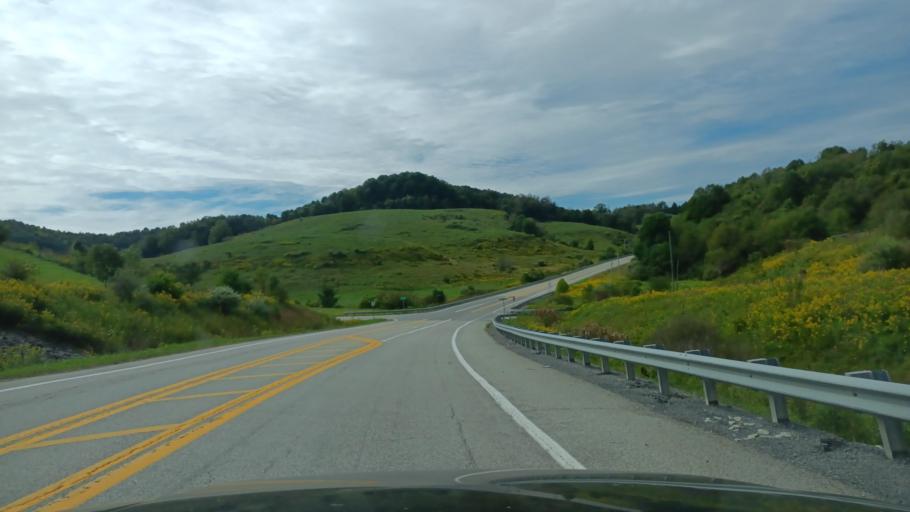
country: US
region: West Virginia
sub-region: Taylor County
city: Grafton
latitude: 39.3150
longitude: -80.1319
